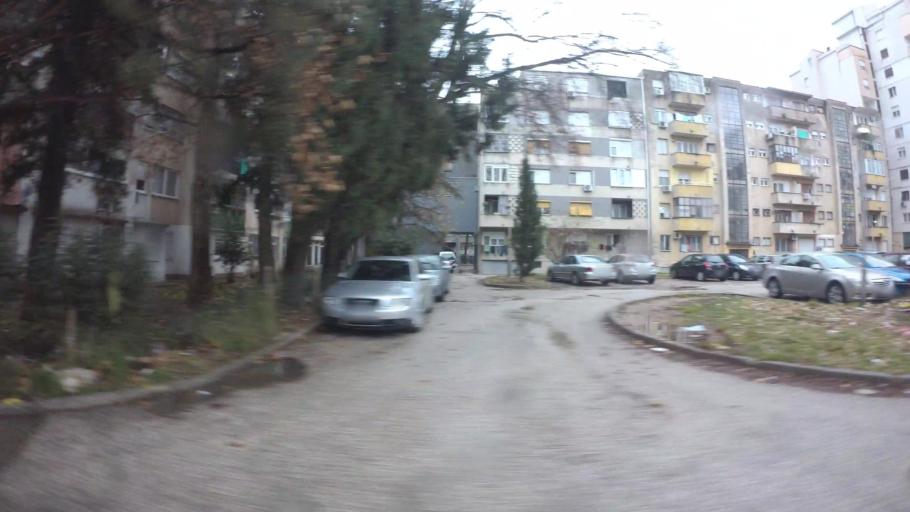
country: BA
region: Federation of Bosnia and Herzegovina
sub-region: Hercegovacko-Bosanski Kanton
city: Mostar
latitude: 43.3448
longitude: 17.7985
